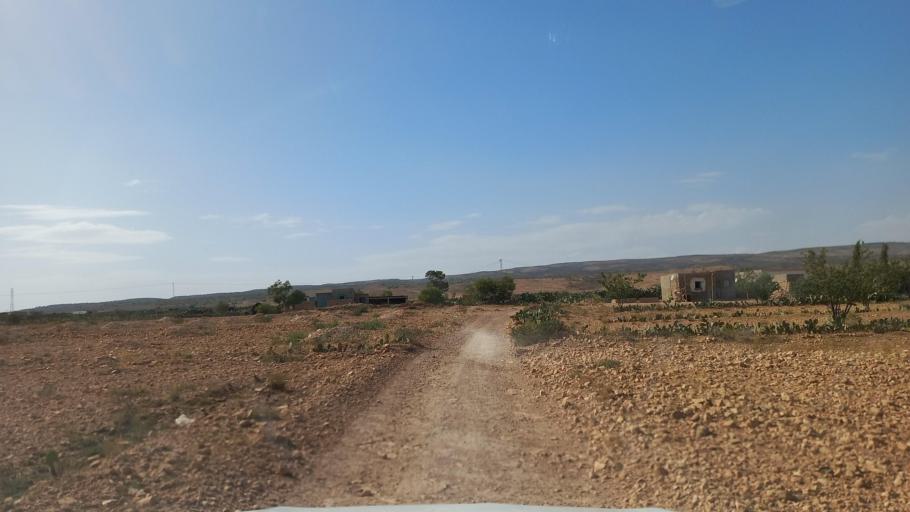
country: TN
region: Al Qasrayn
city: Kasserine
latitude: 35.2860
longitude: 8.9389
